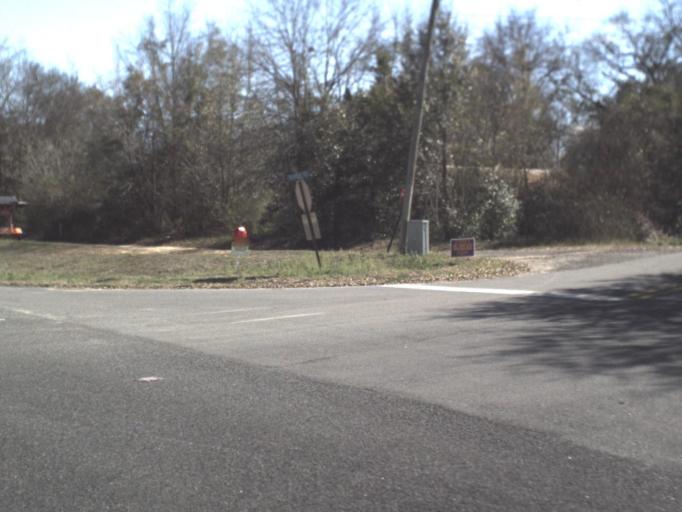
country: US
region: Florida
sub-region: Gadsden County
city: Quincy
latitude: 30.5689
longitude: -84.5472
